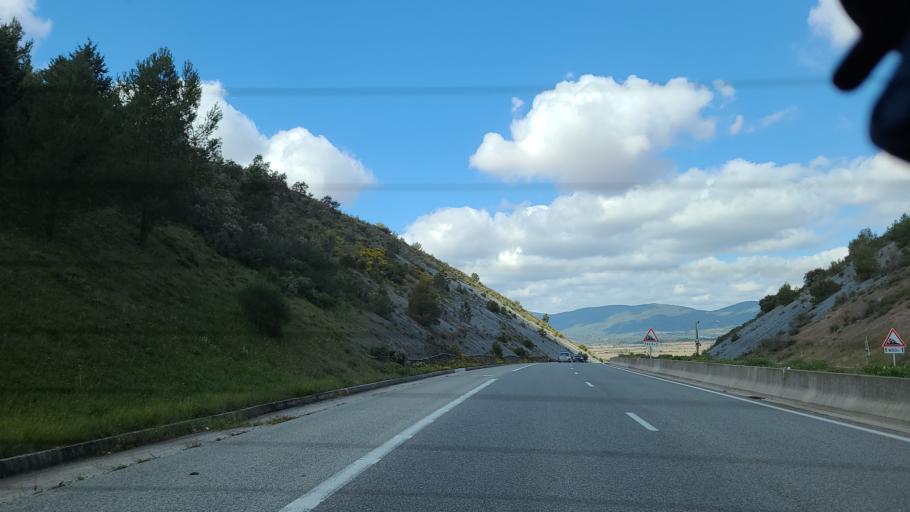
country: FR
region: Provence-Alpes-Cote d'Azur
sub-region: Departement du Var
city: Carnoules
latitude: 43.2700
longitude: 6.1754
